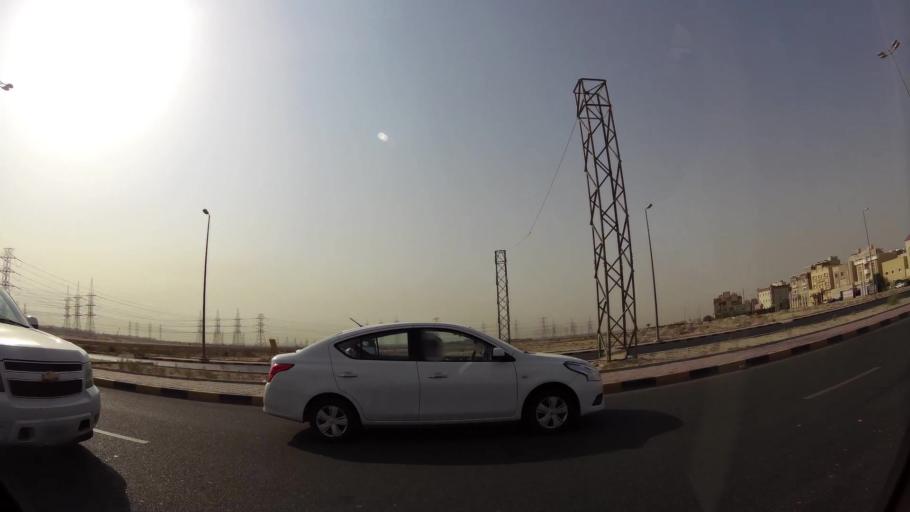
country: KW
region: Muhafazat al Jahra'
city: Al Jahra'
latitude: 29.3399
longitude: 47.7901
